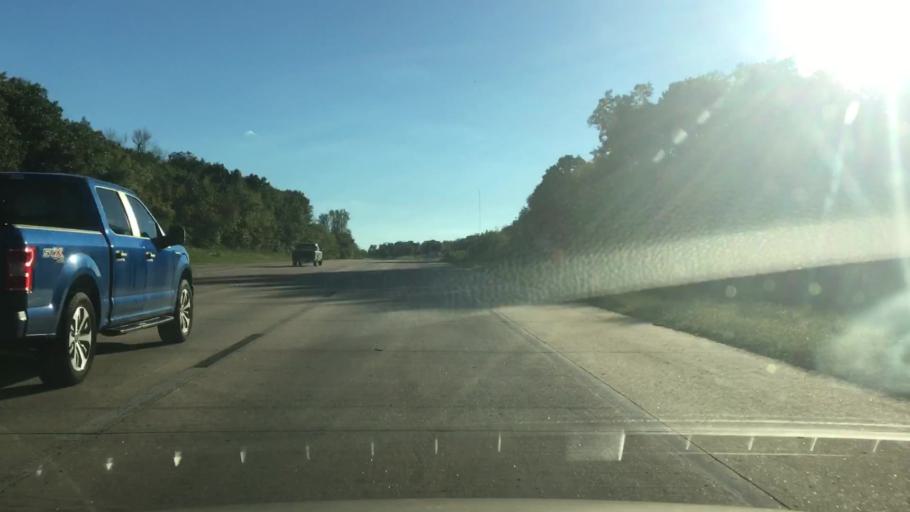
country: US
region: Oklahoma
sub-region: Cherokee County
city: Park Hill
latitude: 35.8383
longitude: -95.0364
